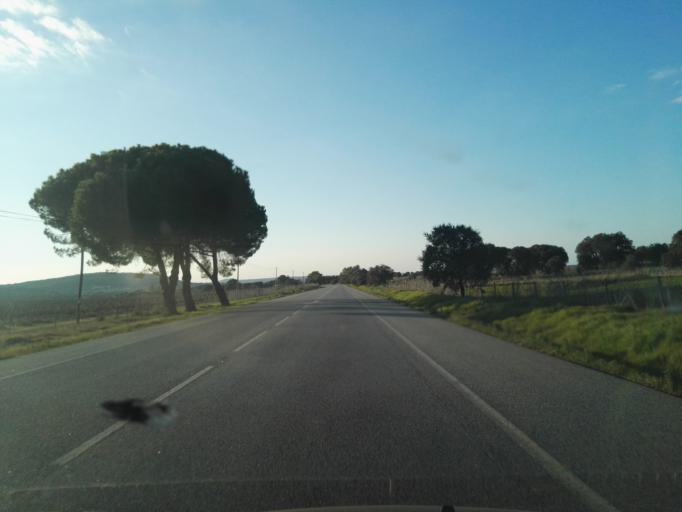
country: PT
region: Evora
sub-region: Montemor-O-Novo
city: Montemor-o-Novo
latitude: 38.6234
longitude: -8.0958
